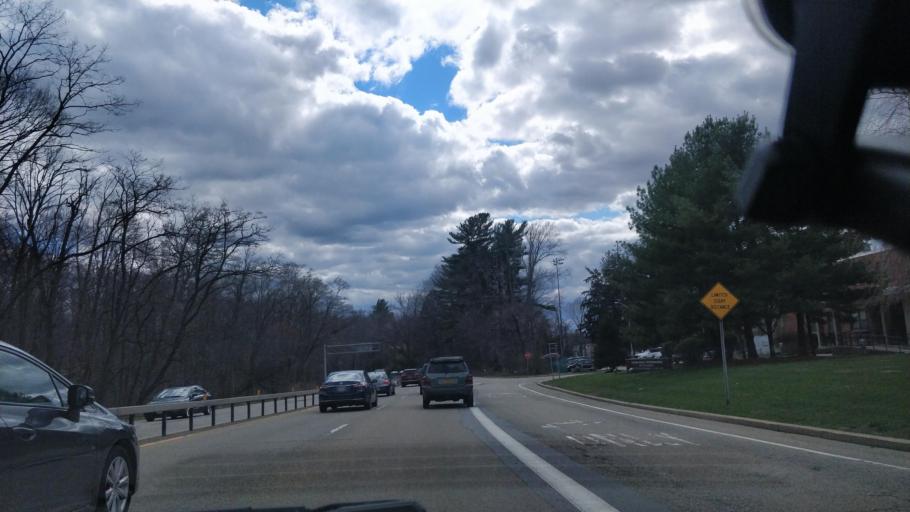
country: US
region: New York
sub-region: Westchester County
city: Ossining
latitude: 41.1789
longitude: -73.8394
